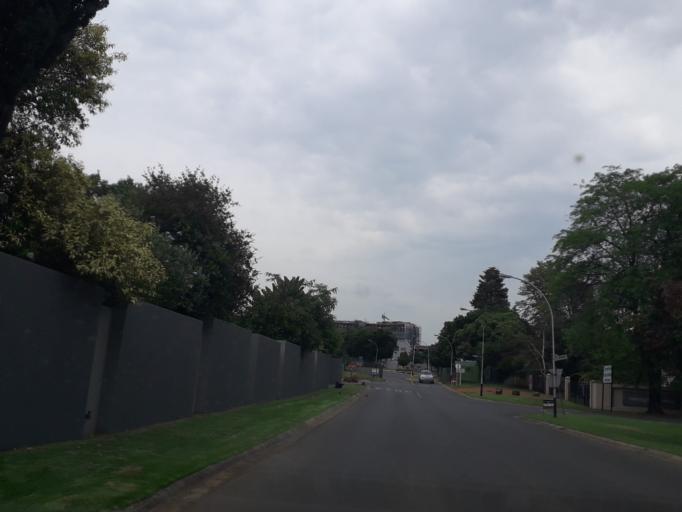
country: ZA
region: Gauteng
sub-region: City of Johannesburg Metropolitan Municipality
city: Johannesburg
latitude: -26.1746
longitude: 28.1157
